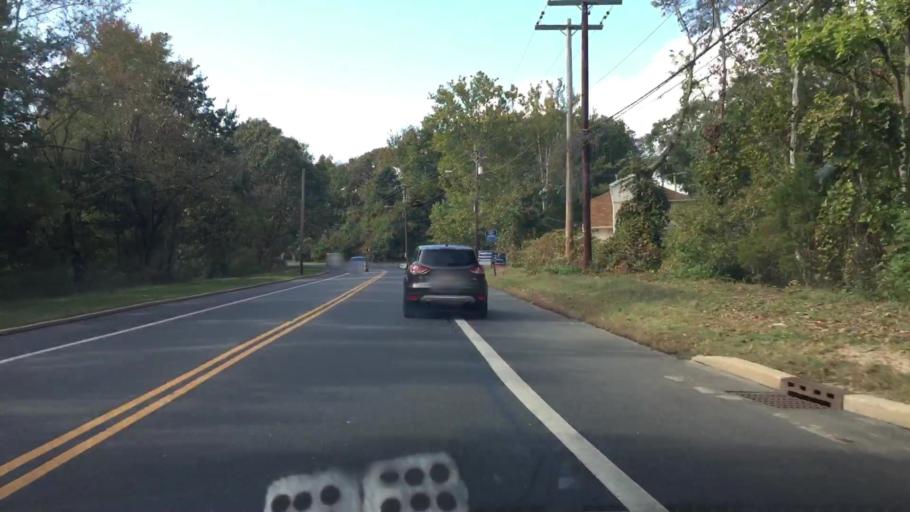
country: US
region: New Jersey
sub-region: Gloucester County
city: Turnersville
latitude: 39.7556
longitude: -75.0574
